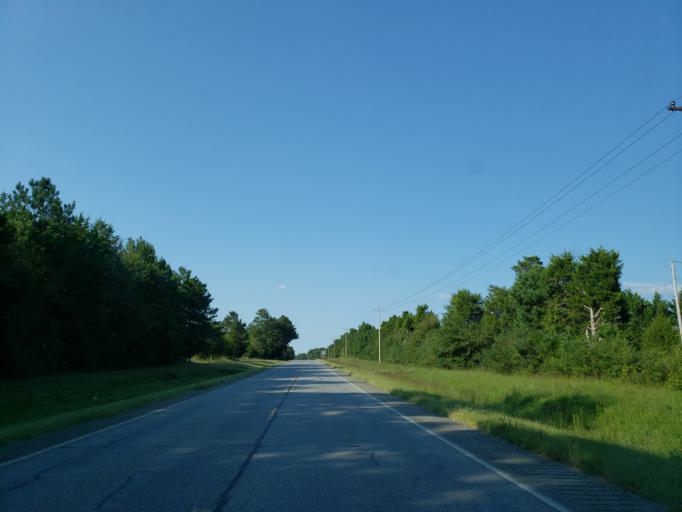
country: US
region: Tennessee
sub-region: Bradley County
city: Wildwood Lake
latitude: 34.9611
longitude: -84.7345
